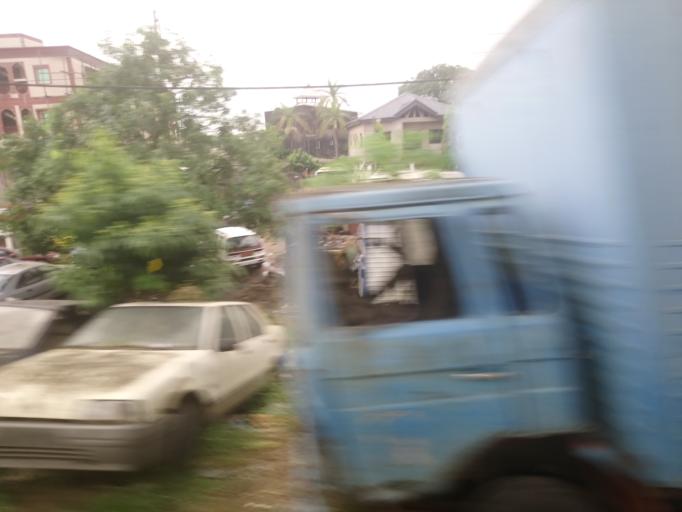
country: CM
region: Littoral
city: Douala
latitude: 4.0204
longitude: 9.7217
